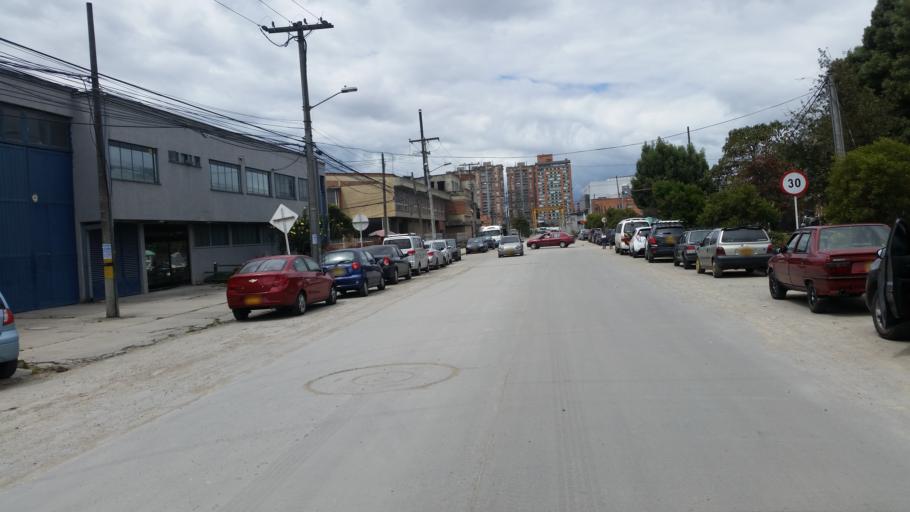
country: CO
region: Bogota D.C.
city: Bogota
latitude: 4.6371
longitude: -74.1096
